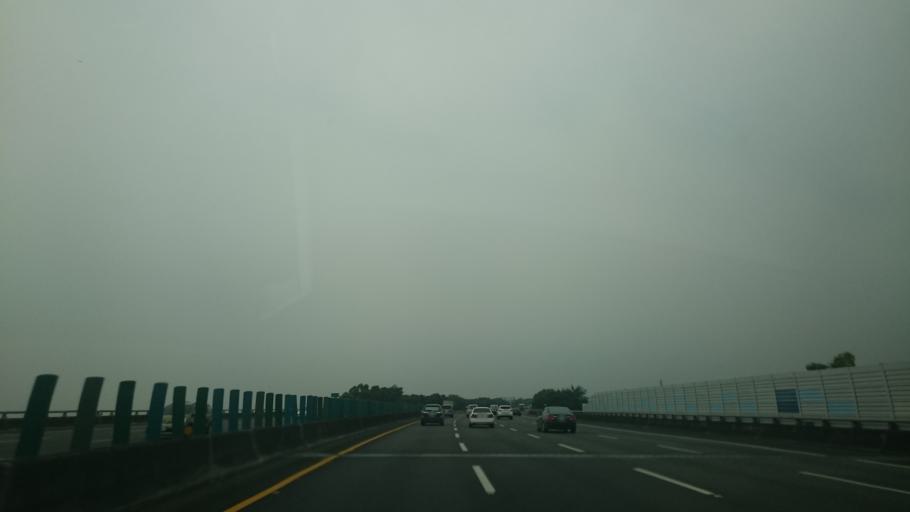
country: TW
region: Taiwan
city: Zhongxing New Village
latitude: 23.9714
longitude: 120.6487
